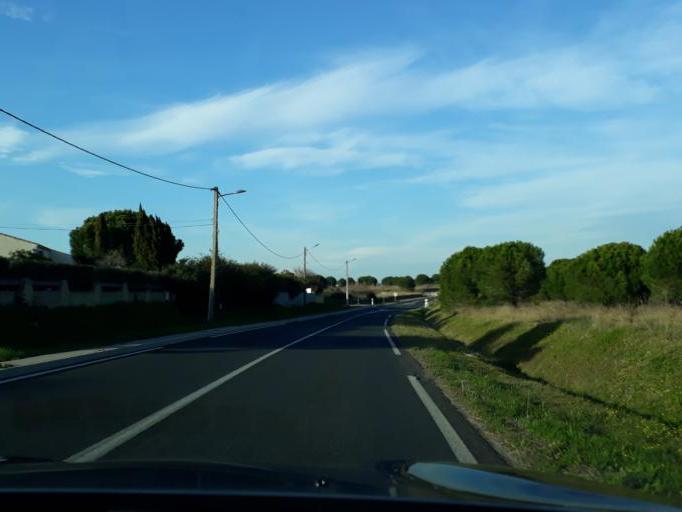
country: FR
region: Languedoc-Roussillon
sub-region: Departement de l'Herault
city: Marseillan
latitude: 43.3382
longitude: 3.5245
